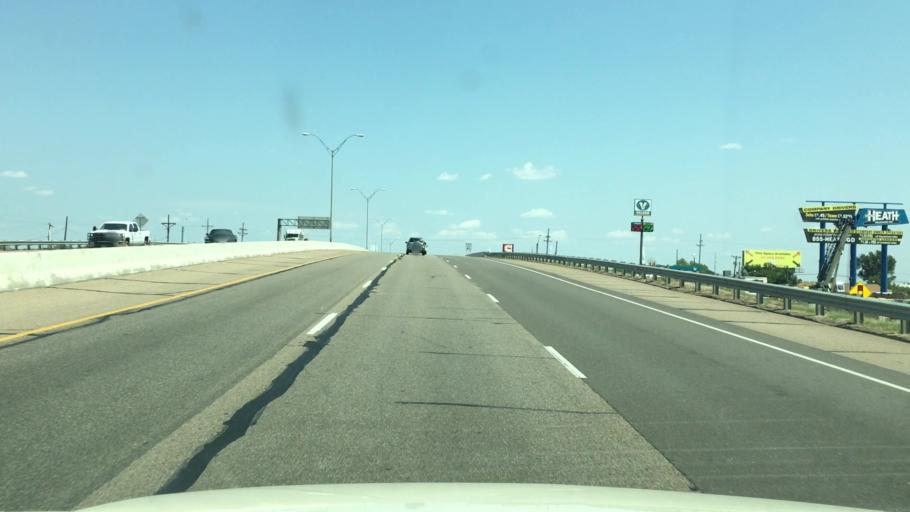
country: US
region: Texas
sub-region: Potter County
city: Amarillo
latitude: 35.1925
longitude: -101.7804
